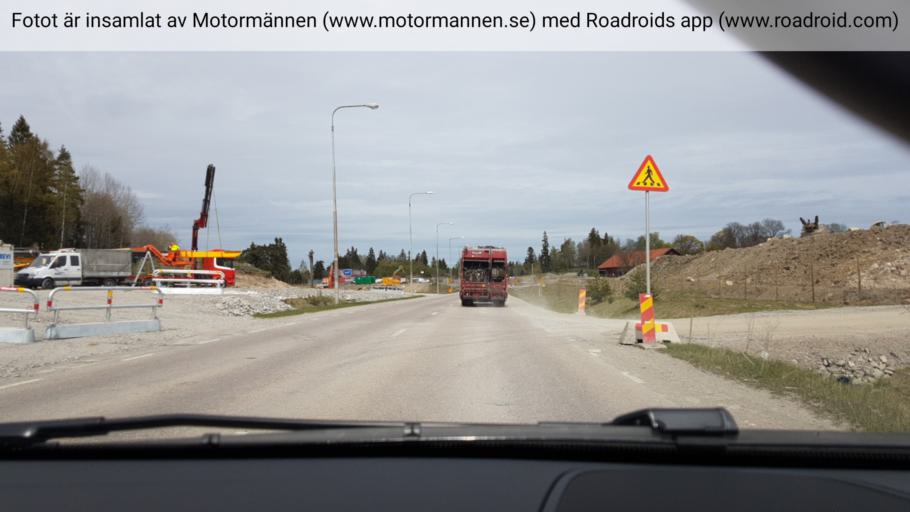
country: SE
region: Stockholm
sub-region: Stockholms Kommun
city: Kista
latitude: 59.4067
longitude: 17.8909
